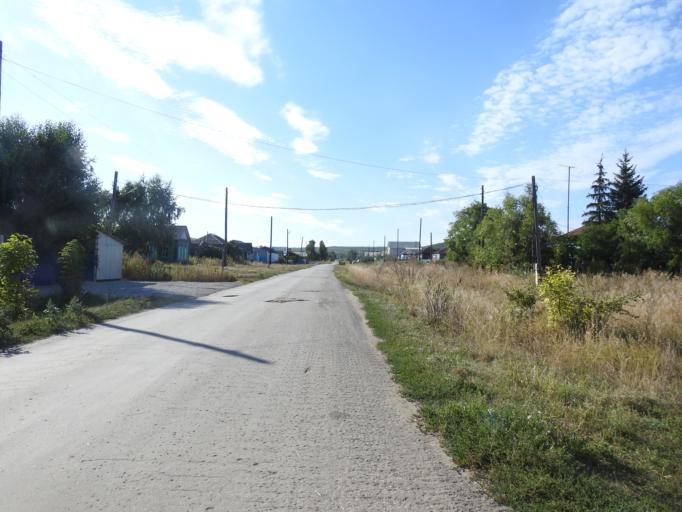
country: RU
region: Saratov
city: Novyye Burasy
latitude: 52.1448
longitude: 46.2542
